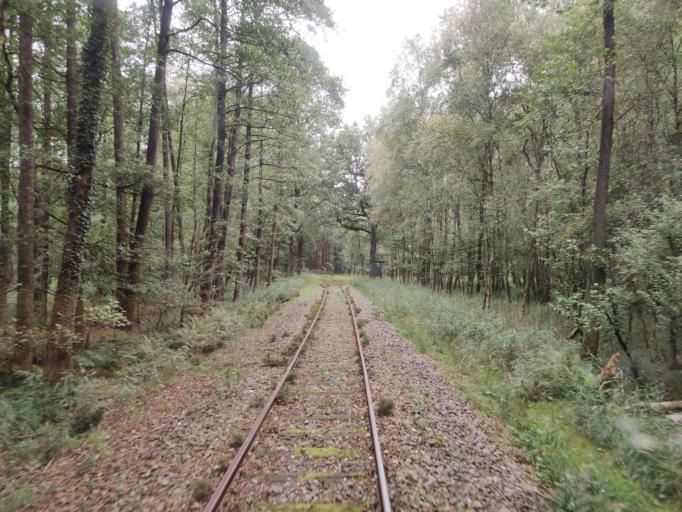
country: DE
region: Lower Saxony
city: Basdahl
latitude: 53.4248
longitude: 9.0179
